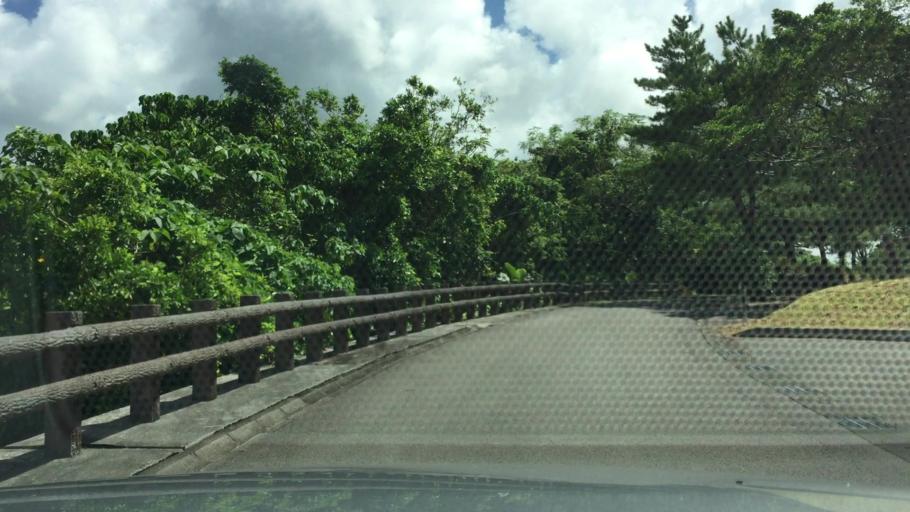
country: JP
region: Okinawa
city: Ishigaki
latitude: 24.3854
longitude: 124.1622
